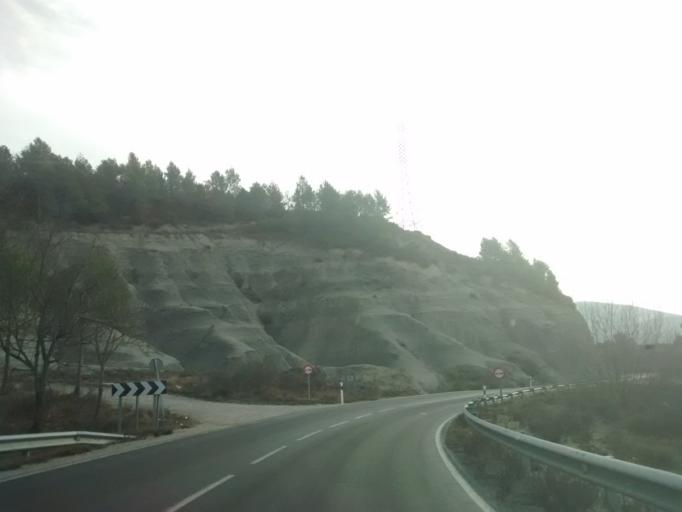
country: ES
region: Aragon
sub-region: Provincia de Zaragoza
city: Undues de Lerda
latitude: 42.6164
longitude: -1.1110
